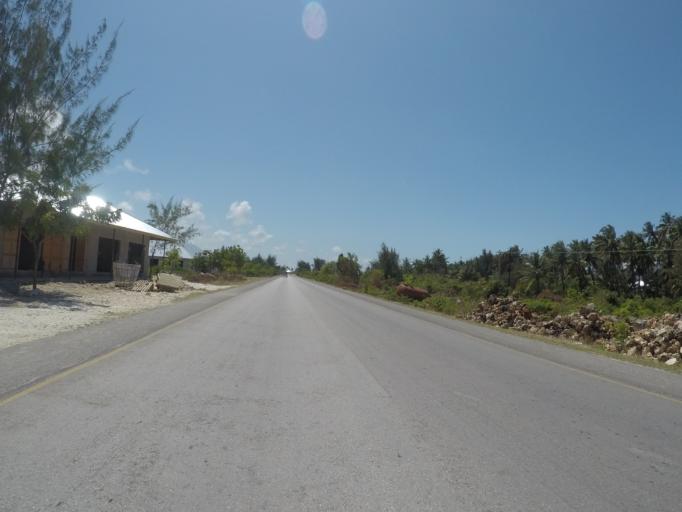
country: TZ
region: Zanzibar Central/South
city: Nganane
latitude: -6.3226
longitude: 39.5449
